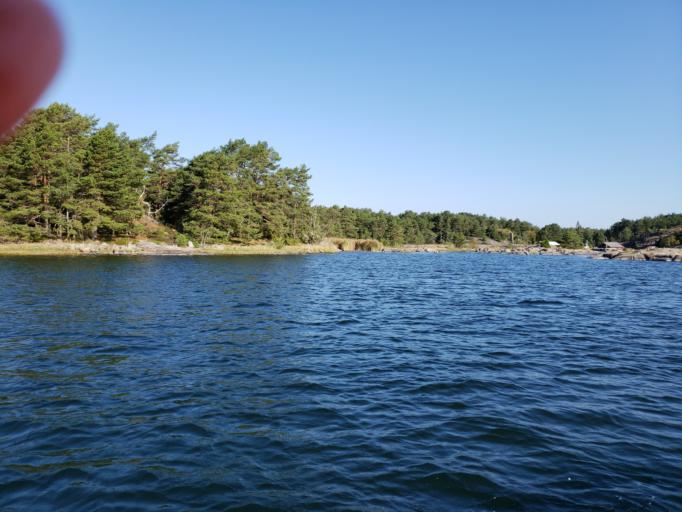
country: FI
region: Varsinais-Suomi
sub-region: Aboland-Turunmaa
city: Dragsfjaerd
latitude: 59.9049
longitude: 22.3661
